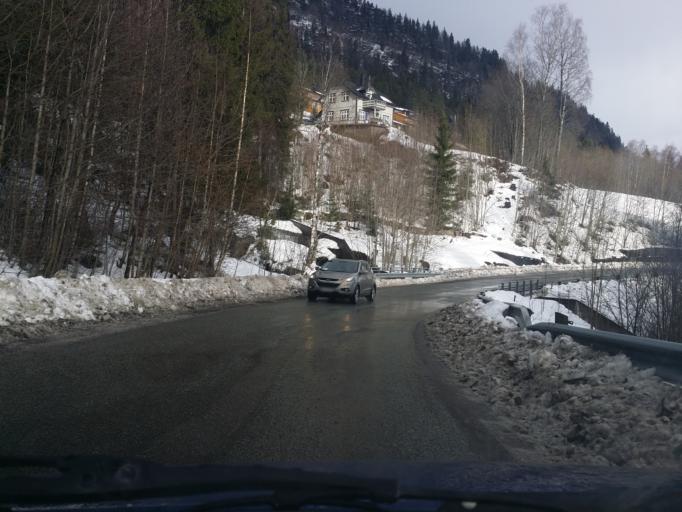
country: NO
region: Buskerud
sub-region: Lier
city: Lierbyen
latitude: 59.8208
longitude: 10.1984
